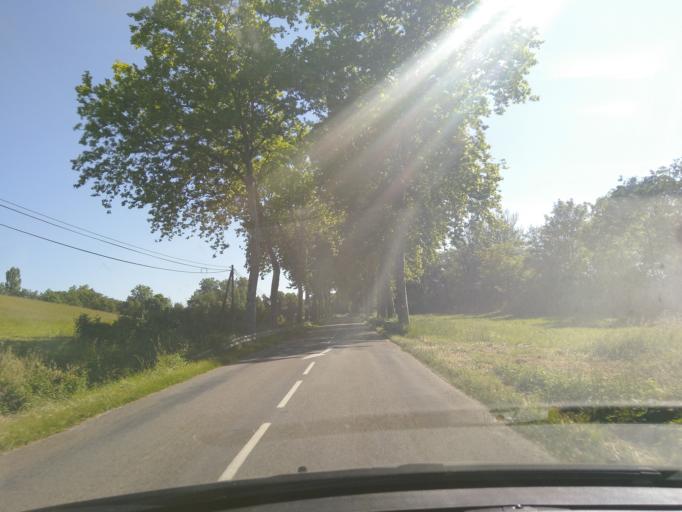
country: FR
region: Midi-Pyrenees
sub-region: Departement du Gers
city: Aubiet
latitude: 43.5411
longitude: 0.7789
